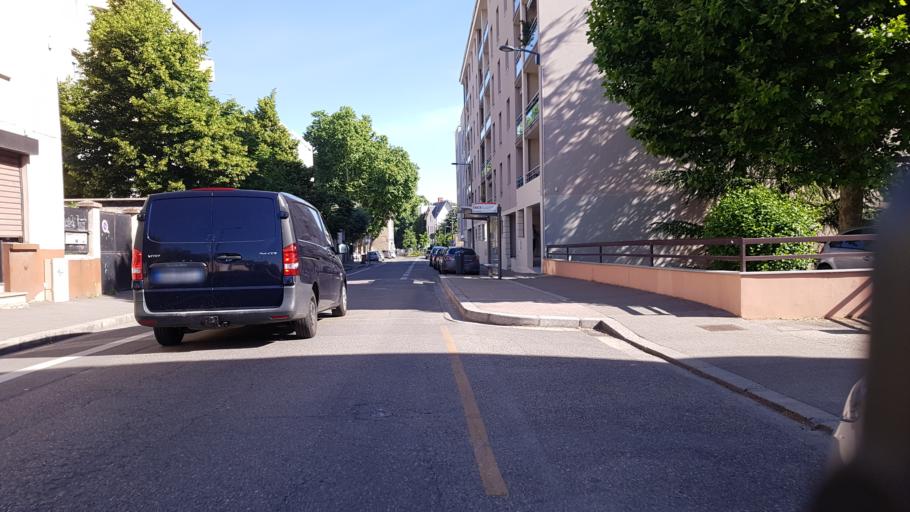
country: FR
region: Rhone-Alpes
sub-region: Departement du Rhone
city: Villeurbanne
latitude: 45.7766
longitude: 4.8842
